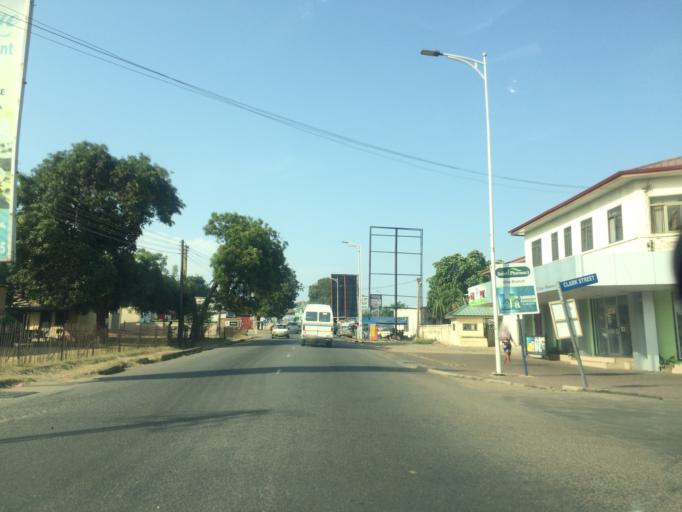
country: GH
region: Greater Accra
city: Accra
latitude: 5.5556
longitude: -0.1831
